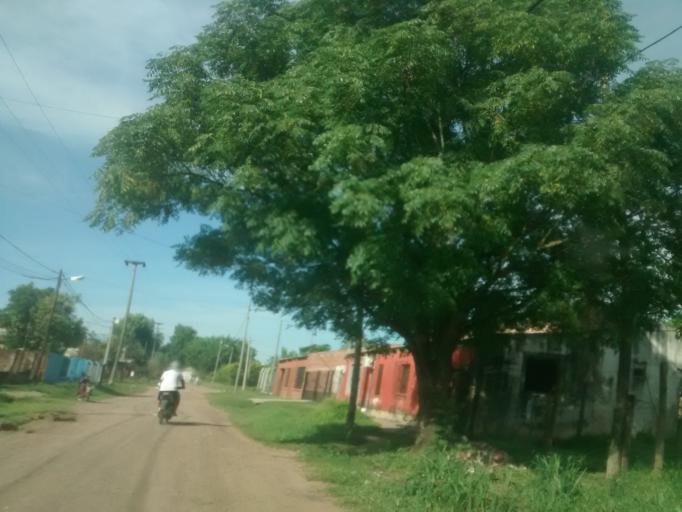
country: AR
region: Chaco
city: Puerto Tirol
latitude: -27.3730
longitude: -59.0925
